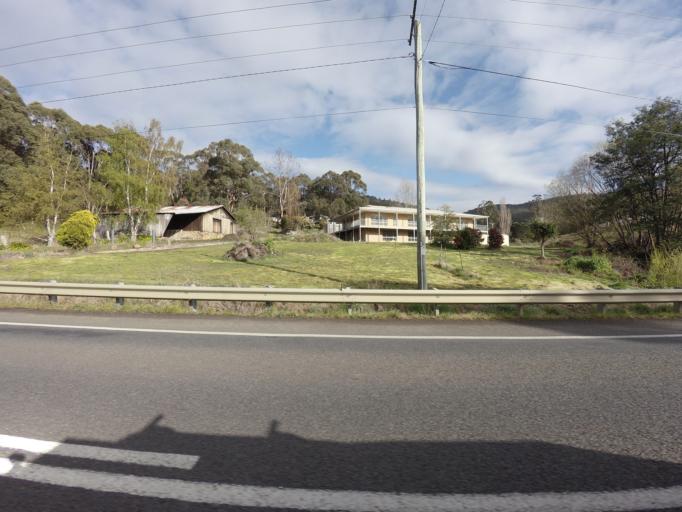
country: AU
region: Tasmania
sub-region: Huon Valley
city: Franklin
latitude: -43.0612
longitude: 147.0279
